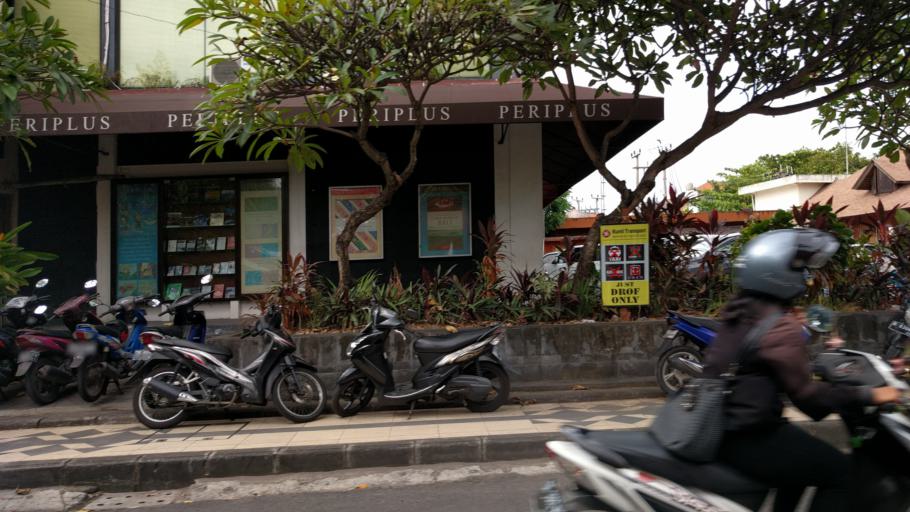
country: ID
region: Bali
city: Kuta
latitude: -8.6887
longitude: 115.1703
